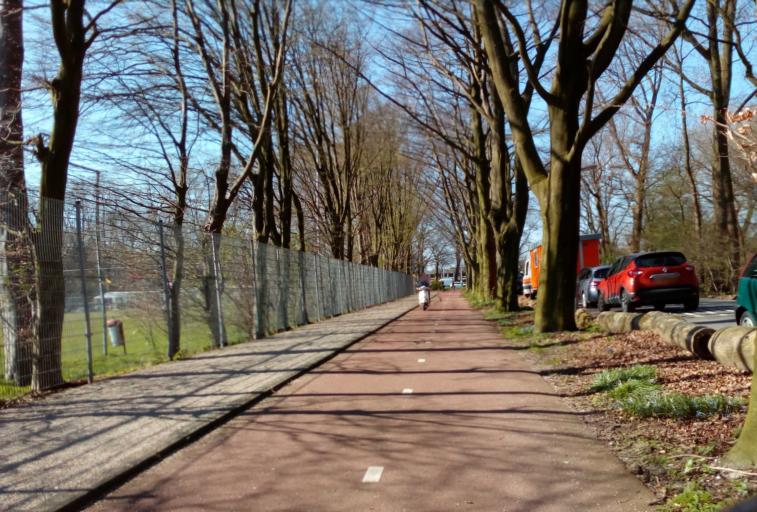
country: NL
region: South Holland
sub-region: Gemeente Rotterdam
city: Rotterdam
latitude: 51.9370
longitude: 4.5033
